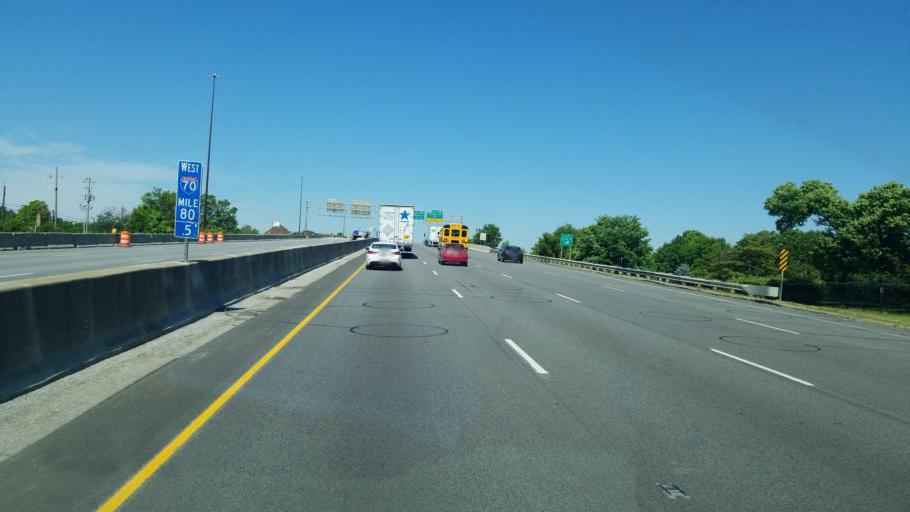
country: US
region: Indiana
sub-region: Marion County
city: Indianapolis
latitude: 39.7530
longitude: -86.1523
